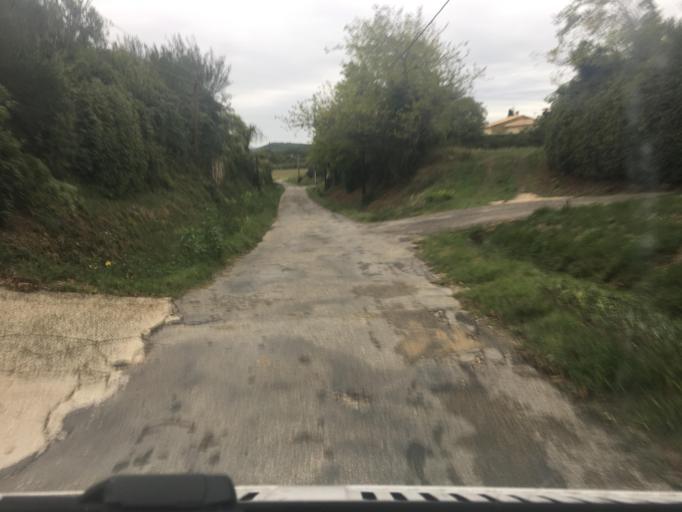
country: FR
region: Languedoc-Roussillon
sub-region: Departement du Gard
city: Uzes
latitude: 44.0207
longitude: 4.4084
